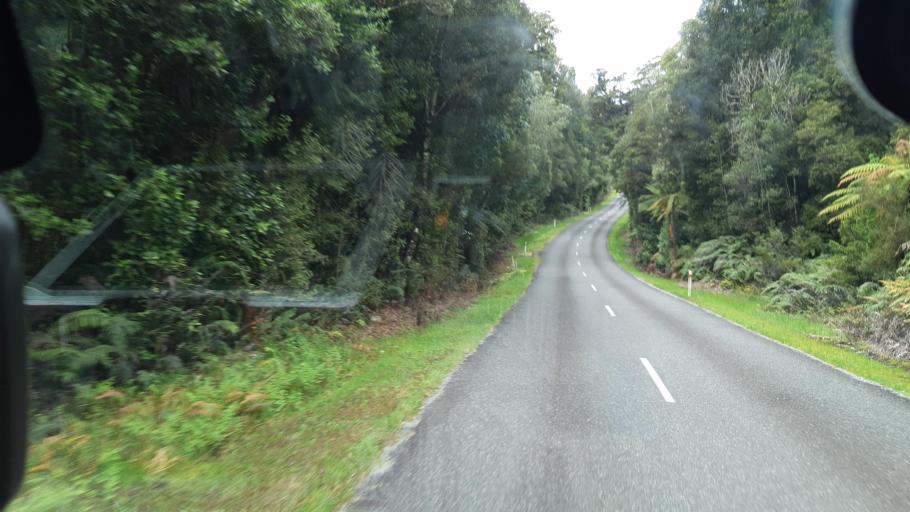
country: NZ
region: West Coast
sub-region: Westland District
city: Hokitika
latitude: -42.7802
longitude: 171.1059
